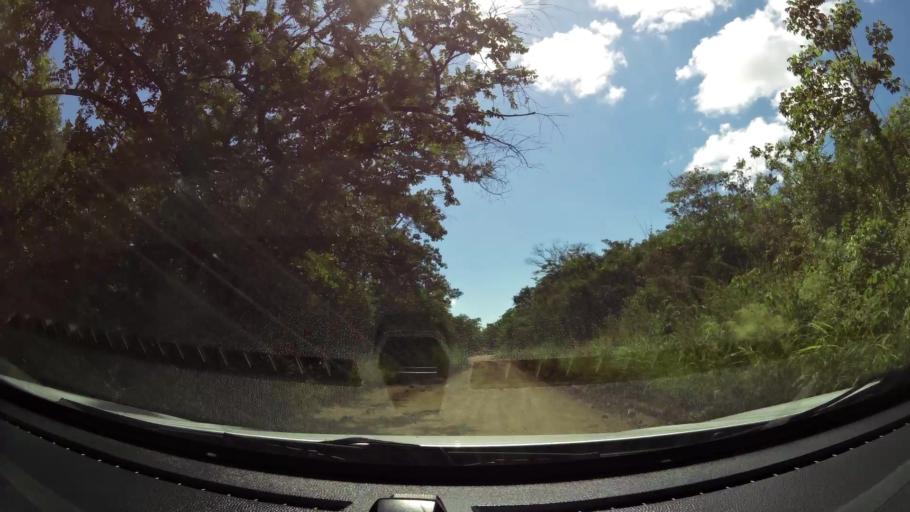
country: CR
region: Guanacaste
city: Bagaces
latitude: 10.5302
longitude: -85.2942
